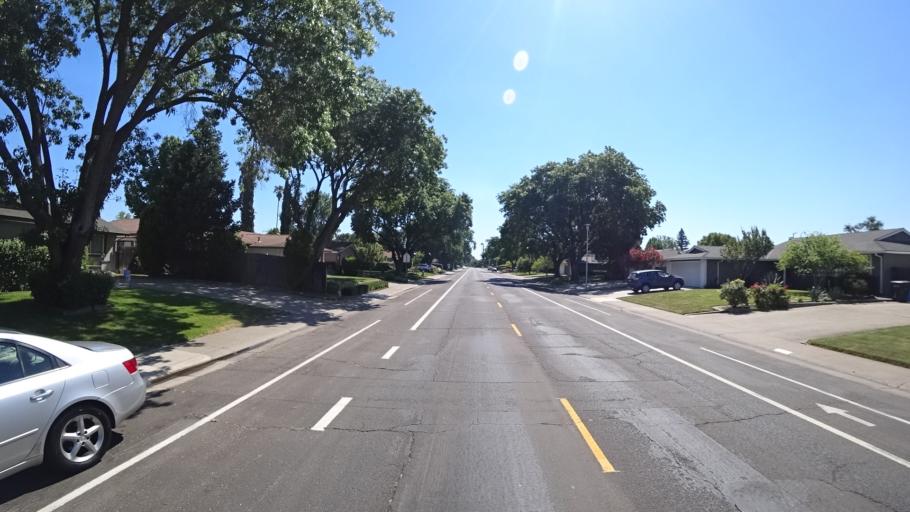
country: US
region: California
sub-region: Sacramento County
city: Rosemont
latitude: 38.5545
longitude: -121.3872
